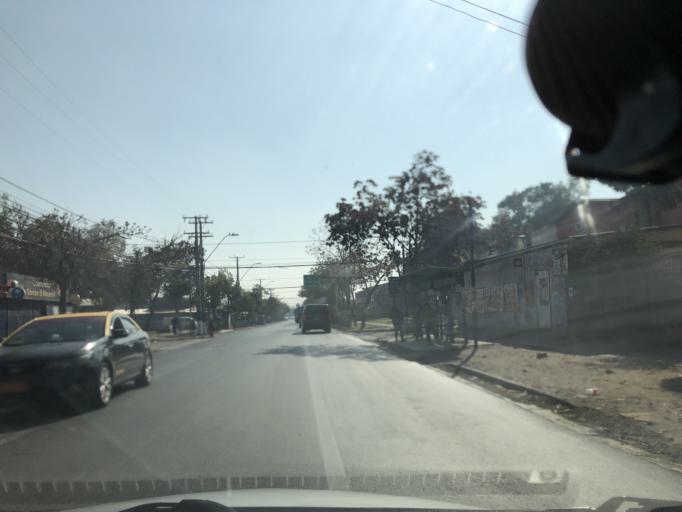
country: CL
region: Santiago Metropolitan
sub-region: Provincia de Cordillera
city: Puente Alto
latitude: -33.5998
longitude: -70.5657
